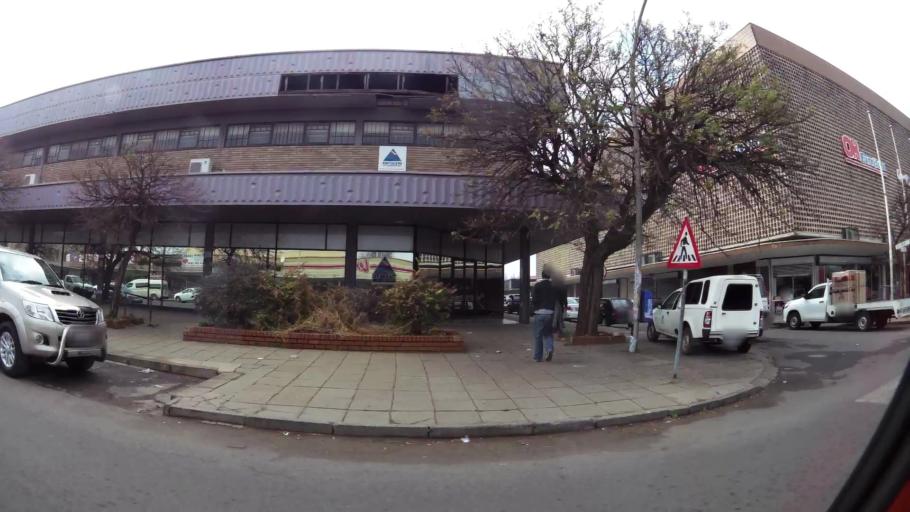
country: ZA
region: Gauteng
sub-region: Sedibeng District Municipality
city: Vanderbijlpark
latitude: -26.6971
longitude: 27.8354
